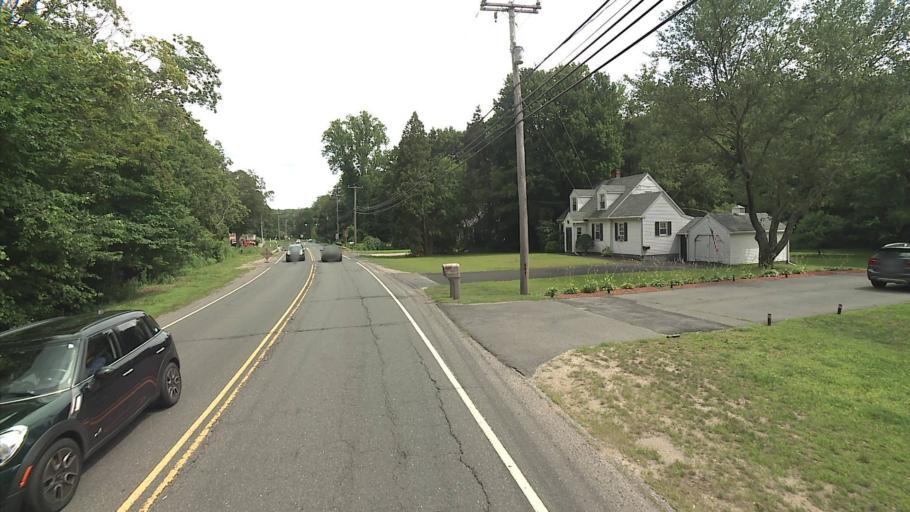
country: US
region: Connecticut
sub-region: New Haven County
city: Oxford
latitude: 41.4334
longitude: -73.1153
